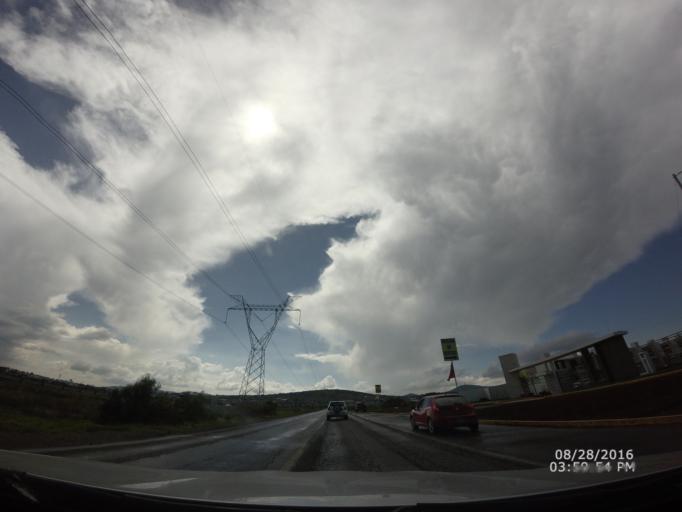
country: MX
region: Hidalgo
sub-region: Zempoala
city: Lindavista
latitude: 20.0388
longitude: -98.7880
